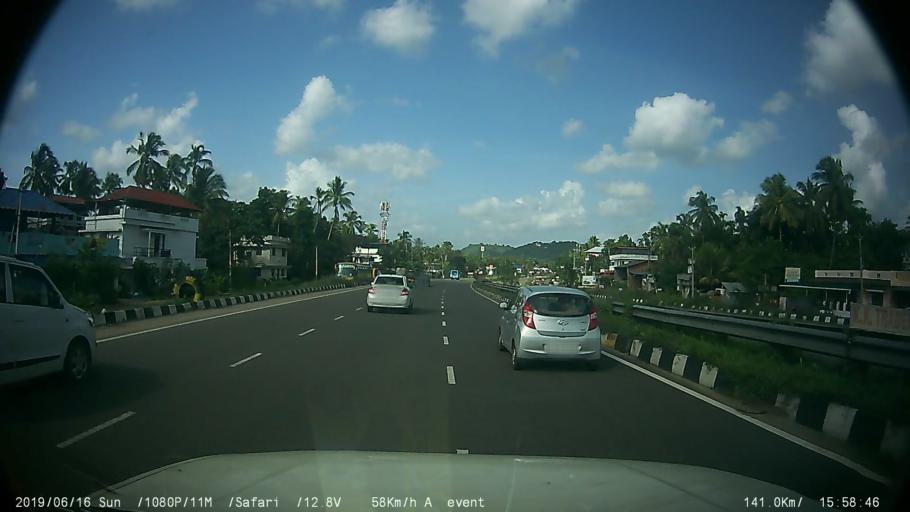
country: IN
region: Kerala
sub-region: Thrissur District
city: Trichur
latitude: 10.5372
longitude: 76.2712
